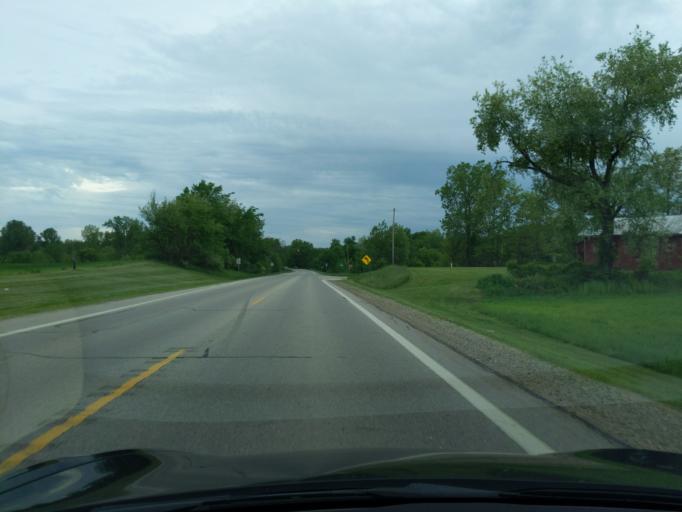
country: US
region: Michigan
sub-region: Jackson County
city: Jackson
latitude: 42.3423
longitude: -84.3476
